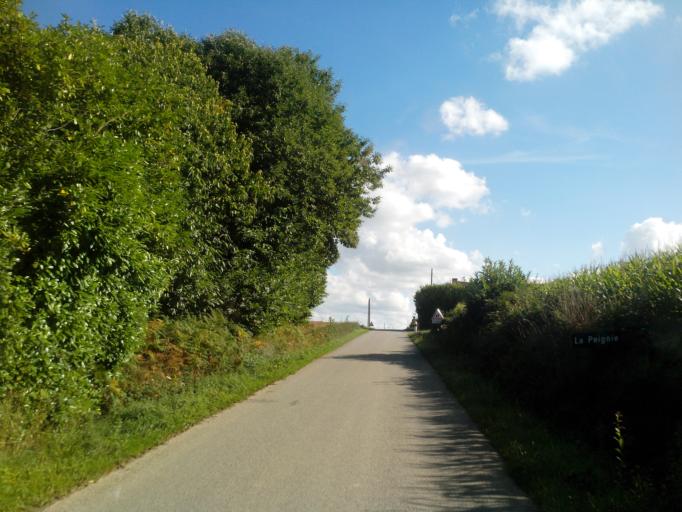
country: FR
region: Brittany
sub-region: Departement des Cotes-d'Armor
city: Merdrignac
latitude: 48.1433
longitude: -2.4020
